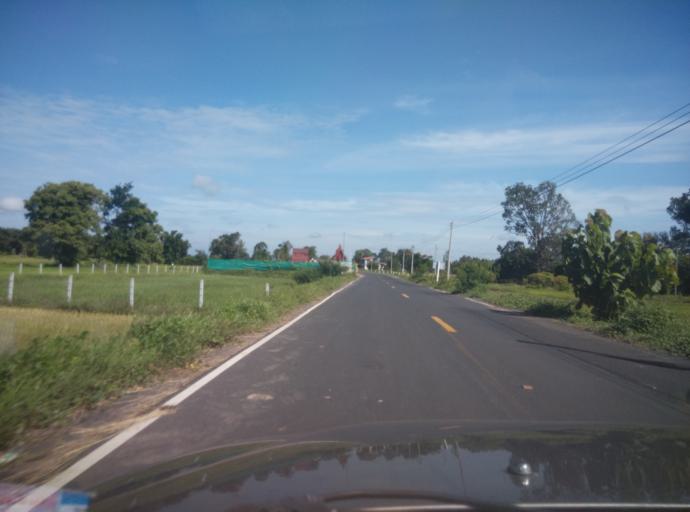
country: TH
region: Sisaket
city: Si Sa Ket
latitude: 15.1181
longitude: 104.2536
